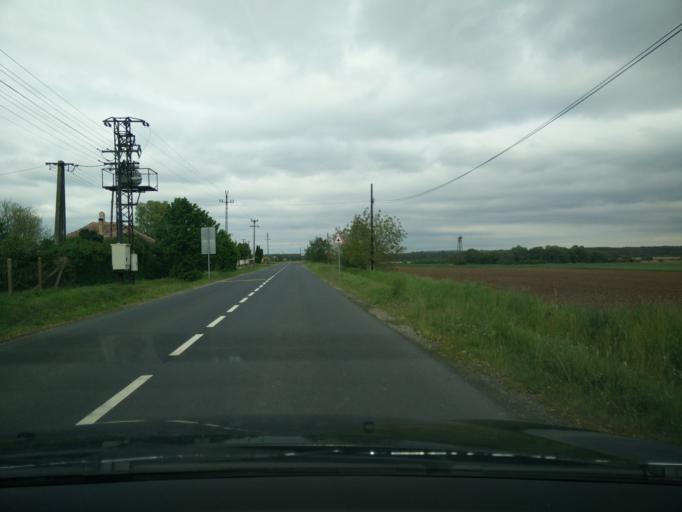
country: HU
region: Zala
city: Zalaszentgrot
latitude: 46.9899
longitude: 17.0368
